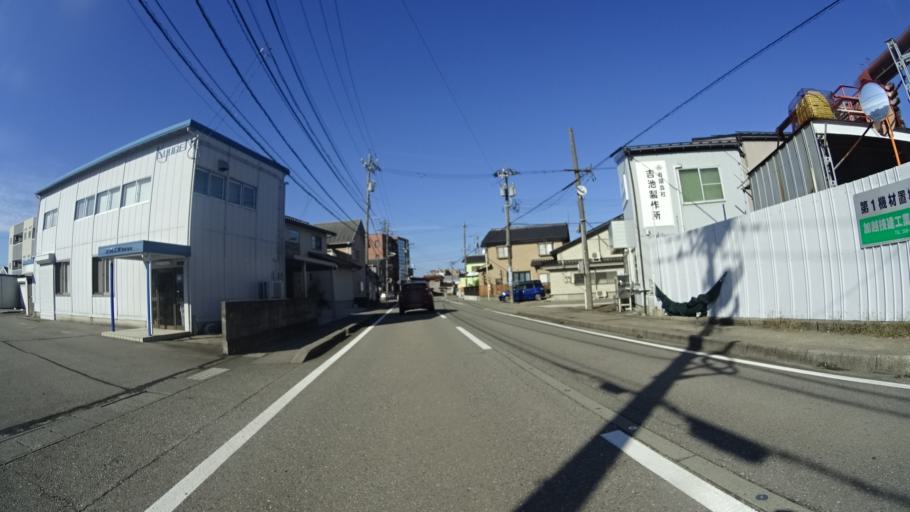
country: JP
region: Ishikawa
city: Kanazawa-shi
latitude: 36.6008
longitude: 136.6079
